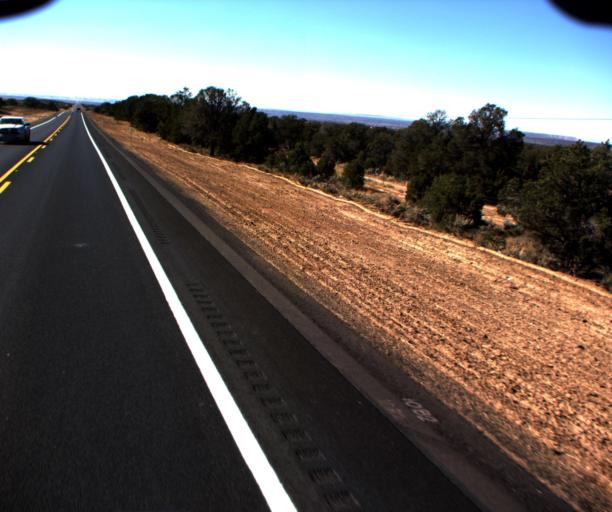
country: US
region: Arizona
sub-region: Apache County
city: Ganado
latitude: 35.7185
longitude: -109.3889
